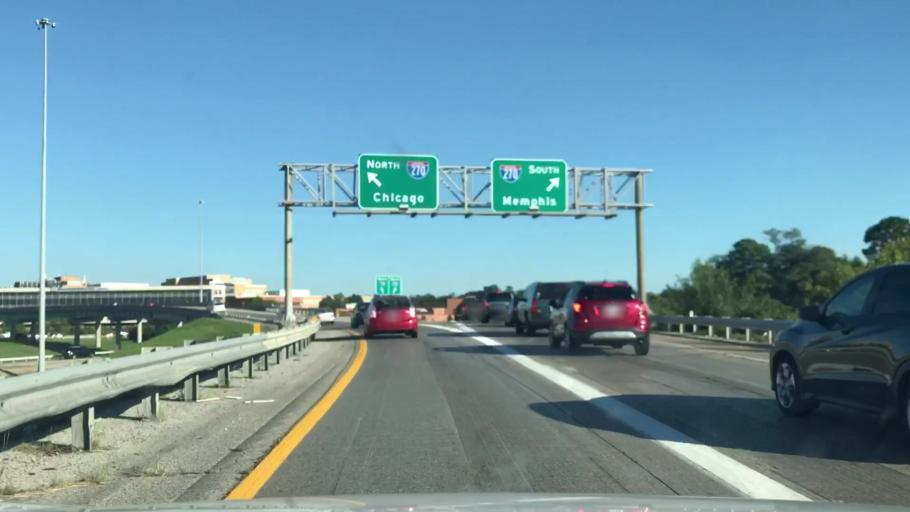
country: US
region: Missouri
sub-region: Saint Louis County
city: Town and Country
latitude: 38.6378
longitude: -90.4527
